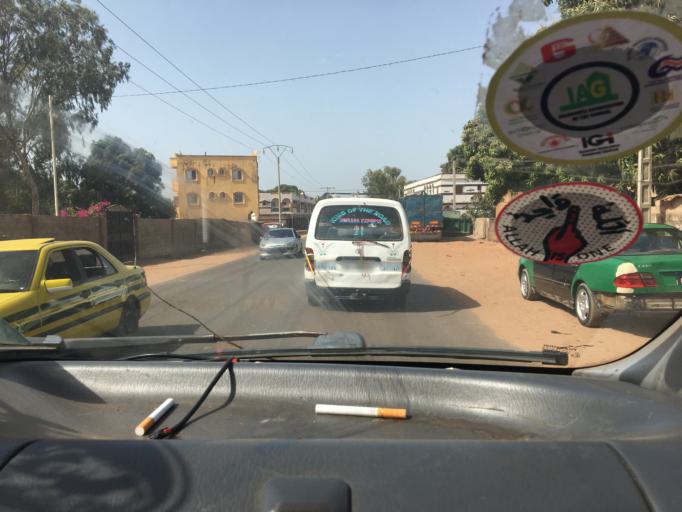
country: GM
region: Western
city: Abuko
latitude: 13.3813
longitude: -16.6805
